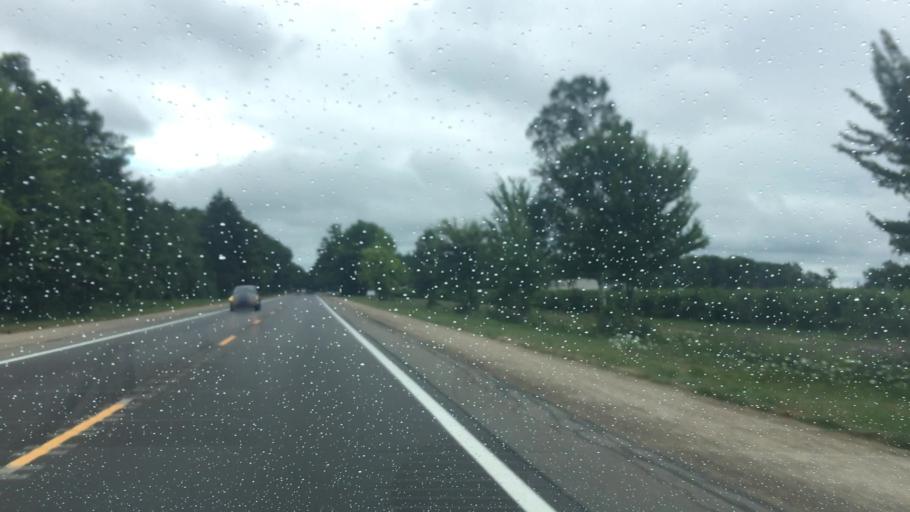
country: US
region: Michigan
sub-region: Ottawa County
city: Spring Lake
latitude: 42.9722
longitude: -86.1516
